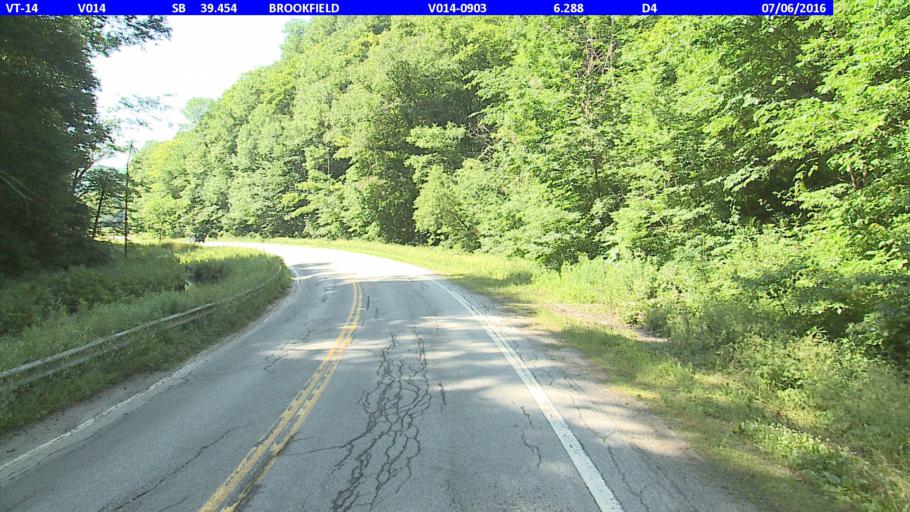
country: US
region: Vermont
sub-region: Orange County
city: Williamstown
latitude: 44.0657
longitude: -72.5679
